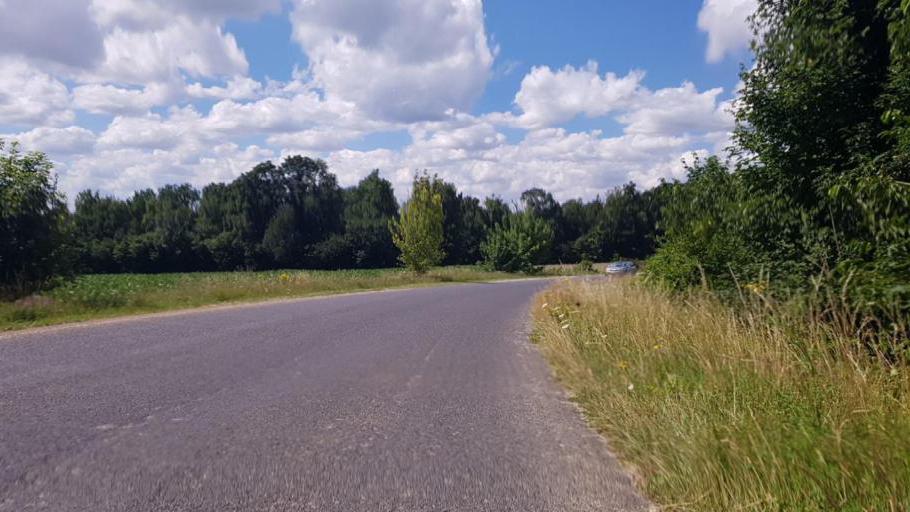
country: FR
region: Lorraine
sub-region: Departement de la Meuse
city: Vacon
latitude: 48.6886
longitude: 5.6764
